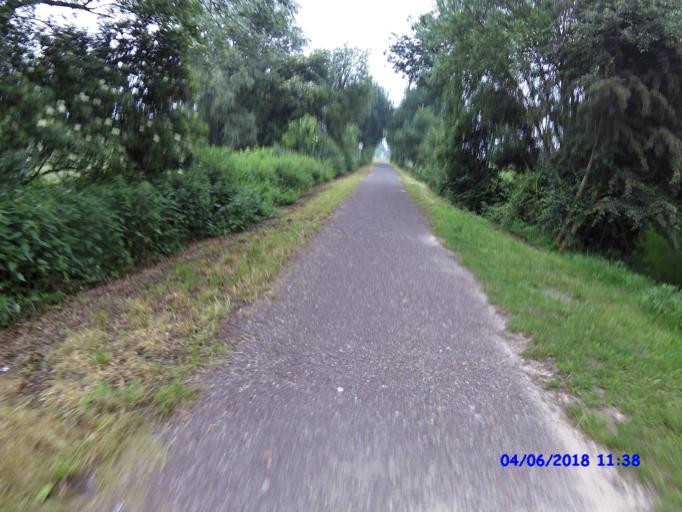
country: BE
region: Flanders
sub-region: Provincie West-Vlaanderen
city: Staden
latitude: 50.9693
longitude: 3.0031
